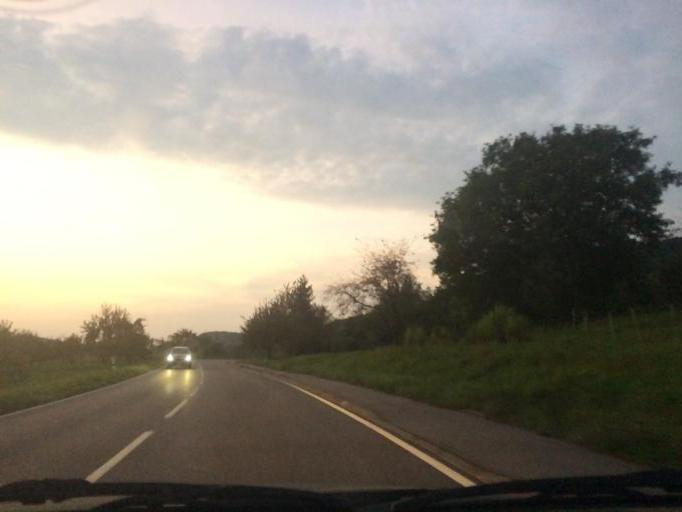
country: DE
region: Baden-Wuerttemberg
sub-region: Regierungsbezirk Stuttgart
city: Schorndorf
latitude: 48.8216
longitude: 9.5246
